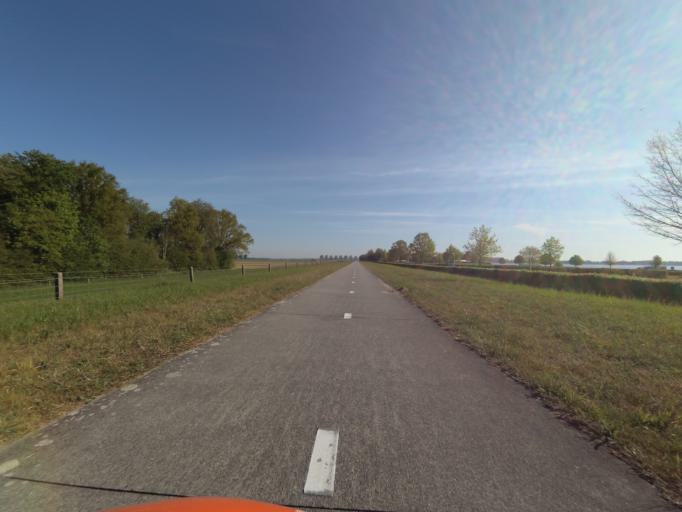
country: NL
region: Gelderland
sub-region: Gemeente Elburg
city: Elburg
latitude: 52.4481
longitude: 5.8031
